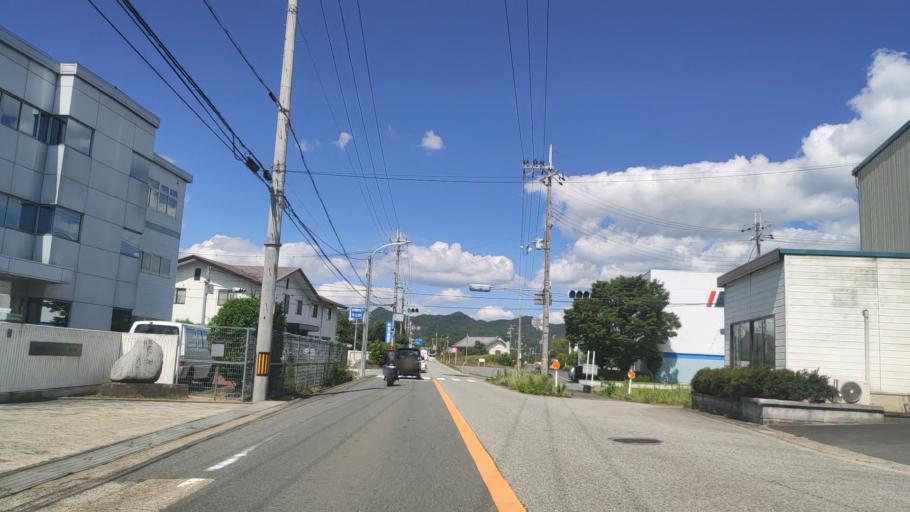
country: JP
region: Kyoto
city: Fukuchiyama
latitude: 35.2239
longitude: 135.1301
